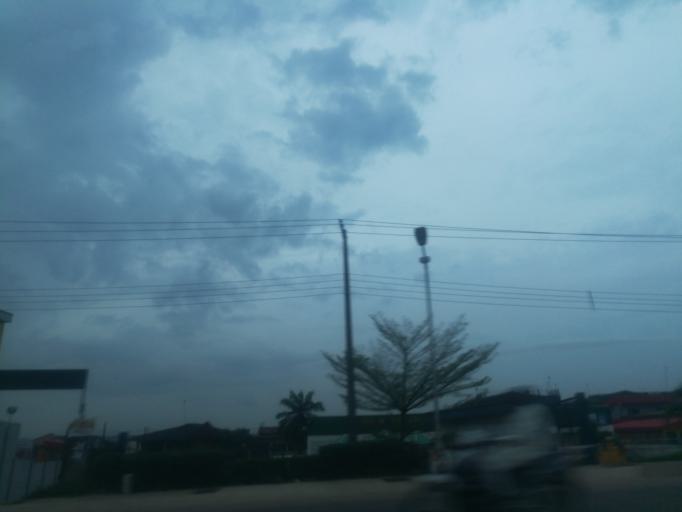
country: NG
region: Oyo
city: Ibadan
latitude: 7.4453
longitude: 3.9069
